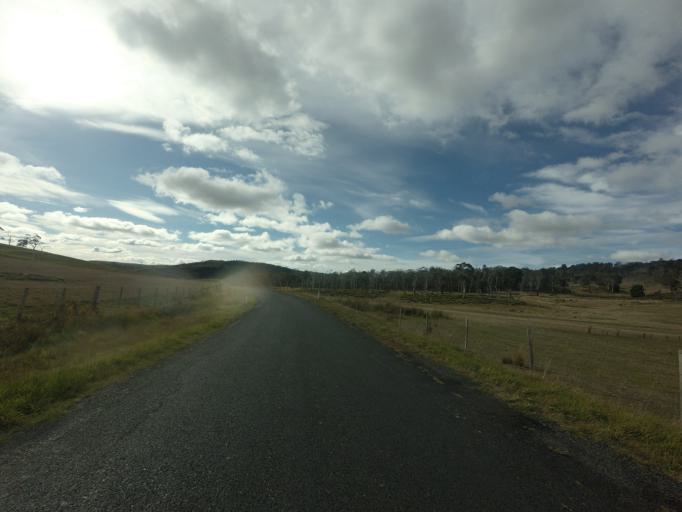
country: AU
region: Tasmania
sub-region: Brighton
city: Bridgewater
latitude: -42.3818
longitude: 147.3615
